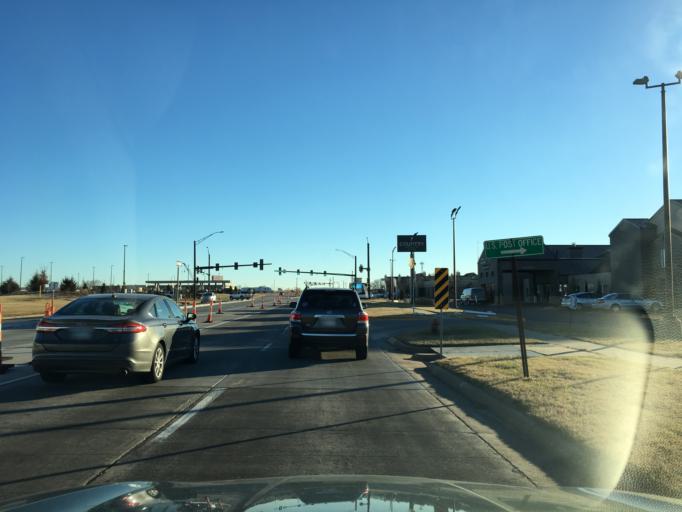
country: US
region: Kansas
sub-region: Sedgwick County
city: Bellaire
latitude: 37.6832
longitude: -97.2263
